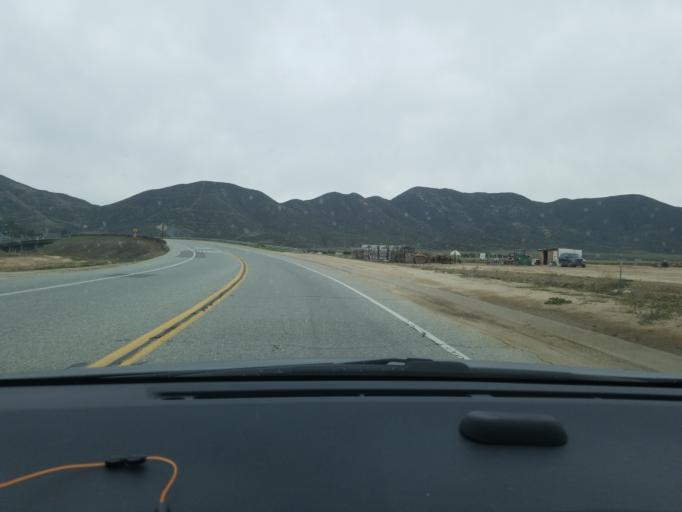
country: US
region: California
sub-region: Riverside County
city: Winchester
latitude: 33.7068
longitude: -117.0362
